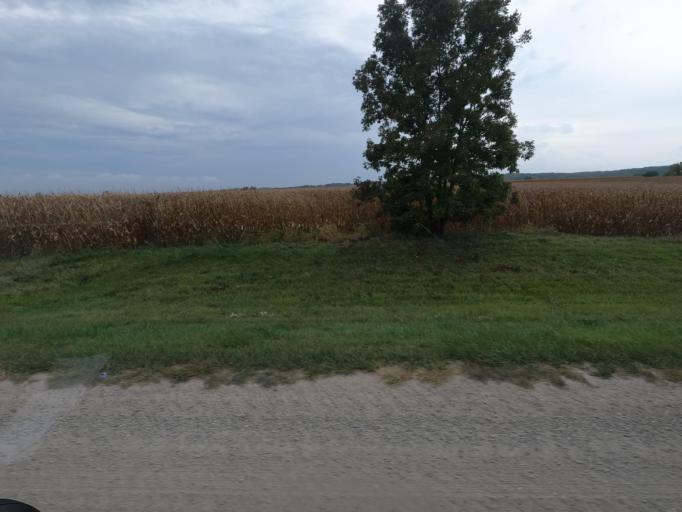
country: US
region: Iowa
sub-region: Van Buren County
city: Keosauqua
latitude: 40.8570
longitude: -92.1096
